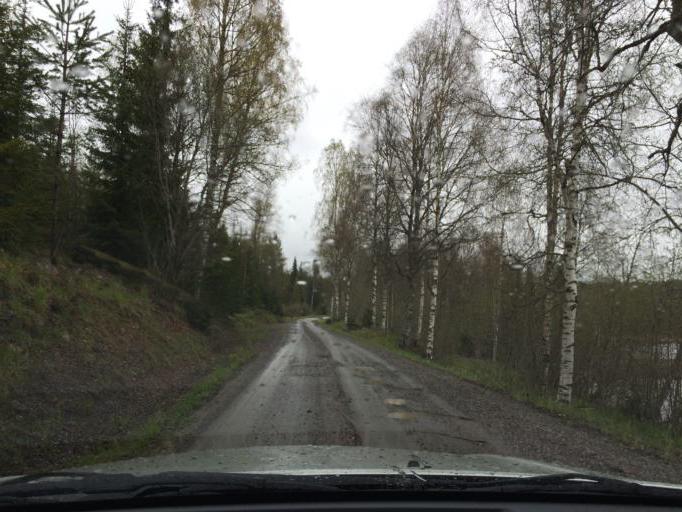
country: SE
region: Dalarna
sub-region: Ludvika Kommun
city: Abborrberget
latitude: 60.0253
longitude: 14.6366
